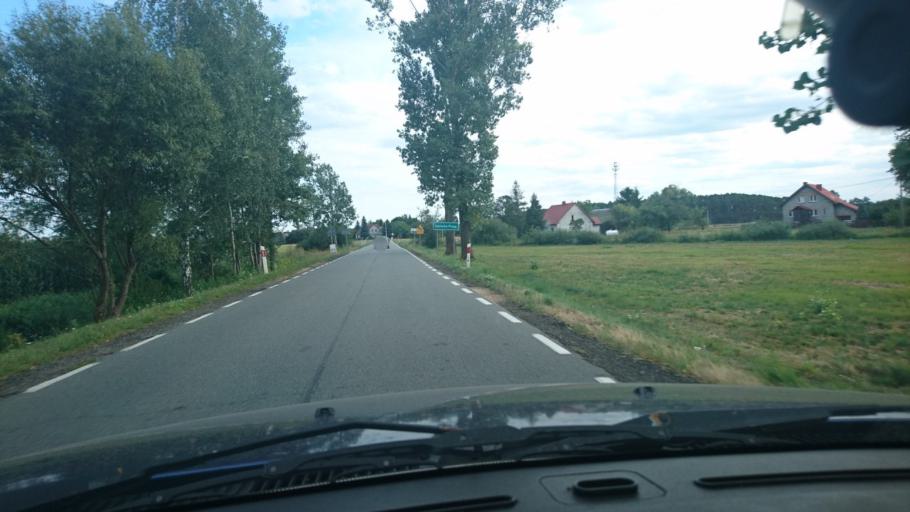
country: PL
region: Greater Poland Voivodeship
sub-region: Powiat ostrowski
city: Przygodzice
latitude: 51.4884
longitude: 17.7884
